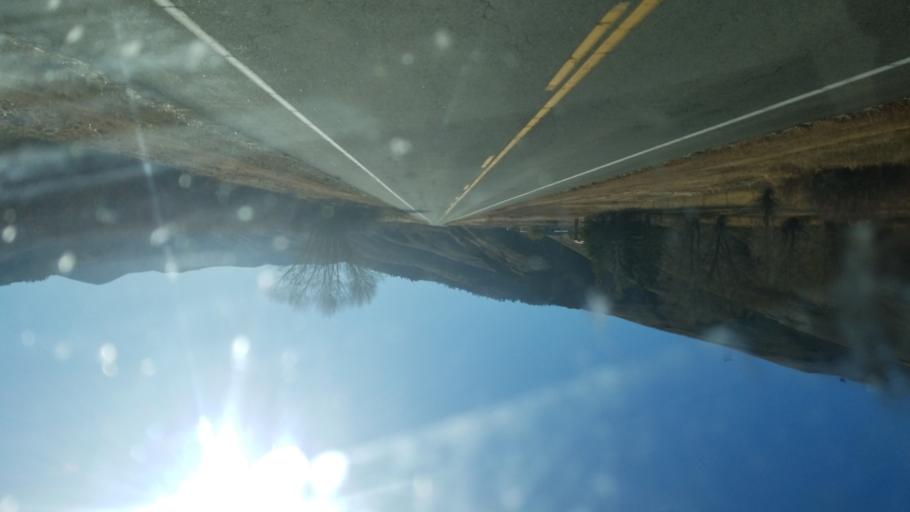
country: US
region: Colorado
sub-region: Gunnison County
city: Gunnison
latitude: 38.4166
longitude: -106.5175
